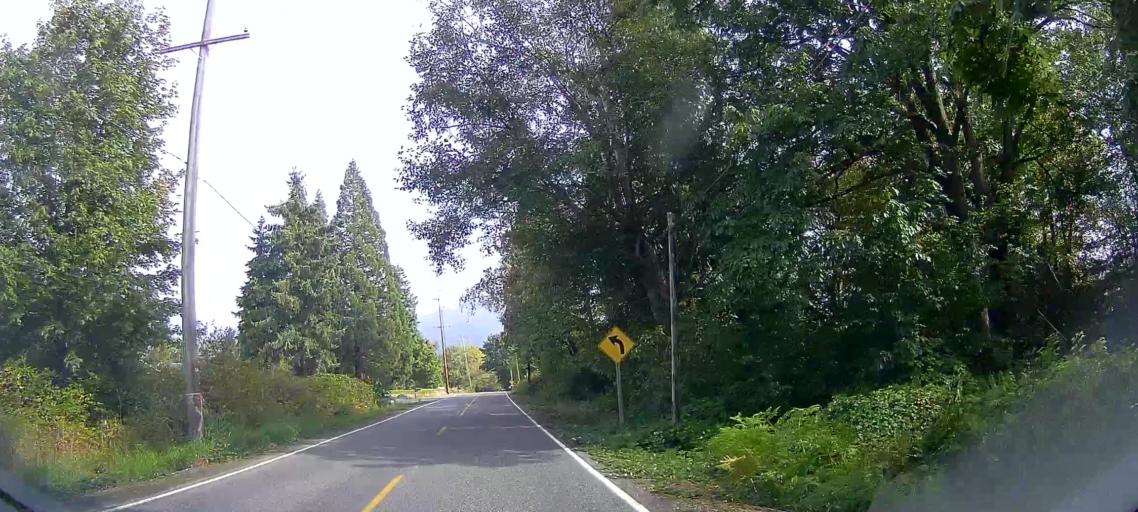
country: US
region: Washington
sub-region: Skagit County
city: Clear Lake
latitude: 48.4544
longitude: -122.2748
